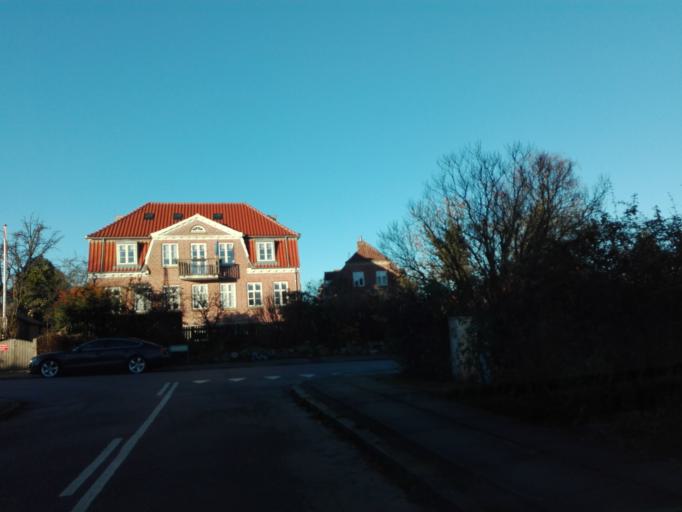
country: DK
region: Central Jutland
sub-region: Arhus Kommune
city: Arhus
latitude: 56.1769
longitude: 10.2153
